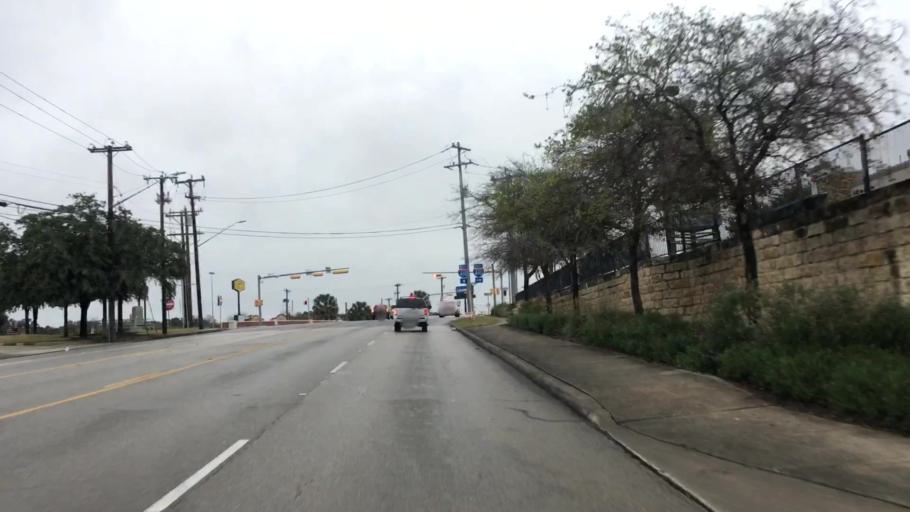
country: US
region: Texas
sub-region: Bexar County
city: Castle Hills
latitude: 29.5192
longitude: -98.5067
